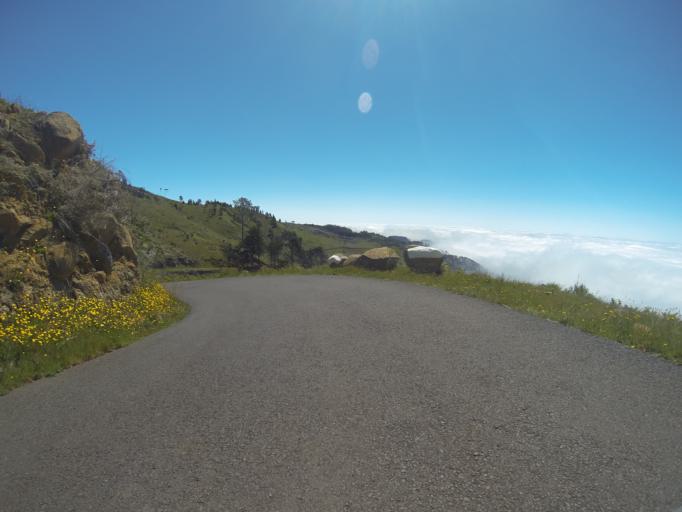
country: PT
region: Madeira
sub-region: Funchal
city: Nossa Senhora do Monte
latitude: 32.7043
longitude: -16.9132
